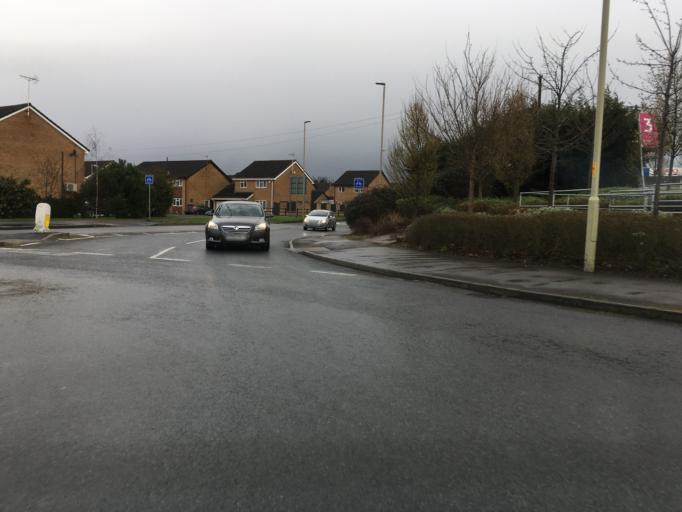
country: GB
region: England
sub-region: Gloucestershire
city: Gloucester
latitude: 51.8286
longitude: -2.2803
